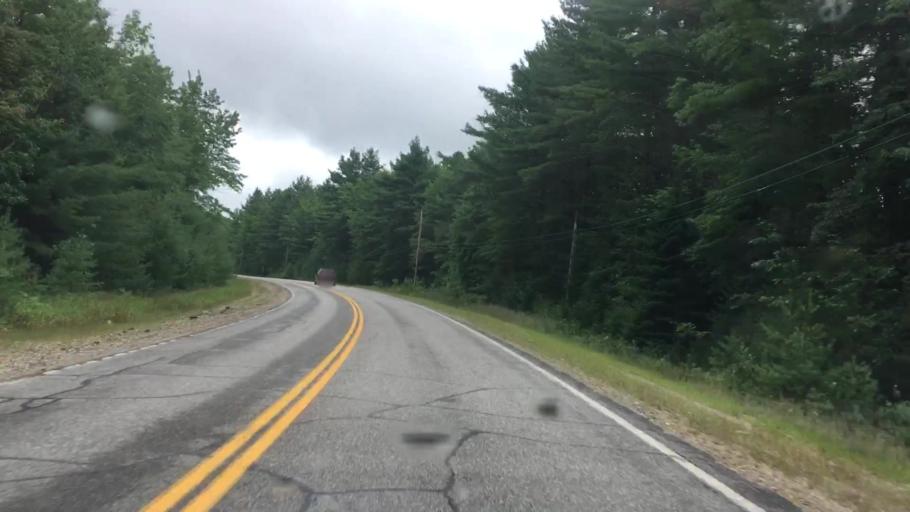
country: US
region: Maine
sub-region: Oxford County
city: Brownfield
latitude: 43.9836
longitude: -70.9319
